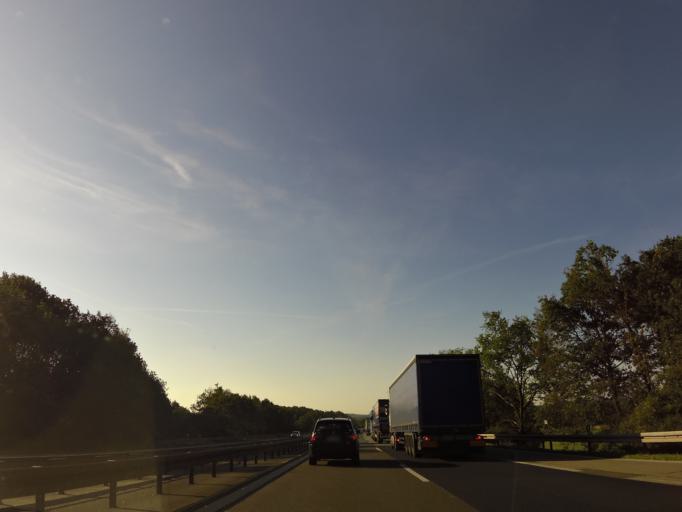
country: DE
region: Bavaria
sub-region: Regierungsbezirk Mittelfranken
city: Gremsdorf
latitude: 49.7113
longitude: 10.8454
